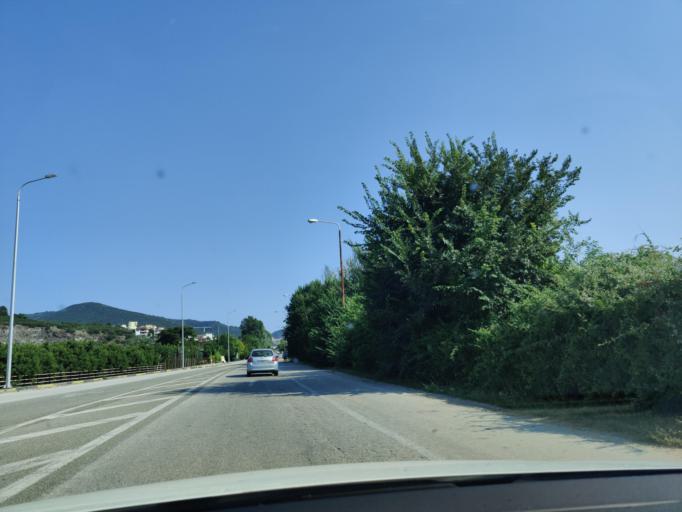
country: GR
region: East Macedonia and Thrace
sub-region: Nomos Kavalas
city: Amygdaleonas
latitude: 40.9697
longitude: 24.3528
